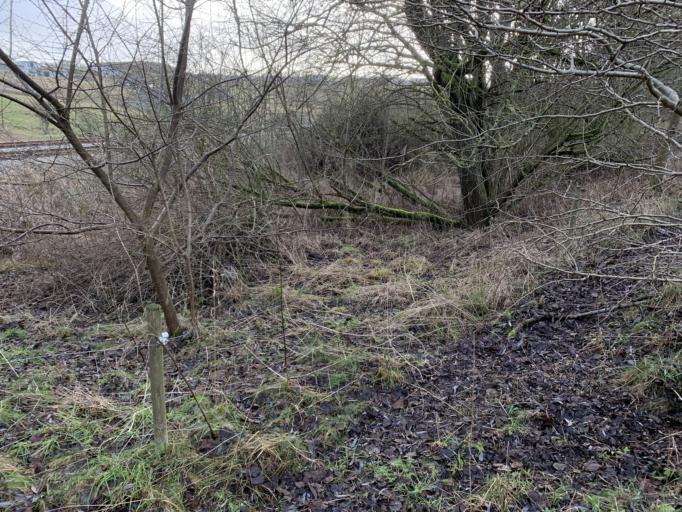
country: DK
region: North Denmark
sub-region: Mariagerfjord Kommune
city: Hobro
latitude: 56.6587
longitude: 9.7866
